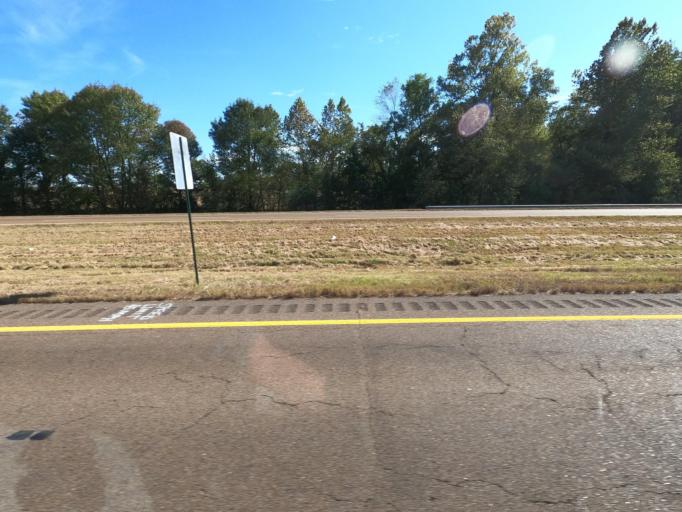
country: US
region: Tennessee
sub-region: Obion County
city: South Fulton
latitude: 36.4717
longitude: -88.9661
